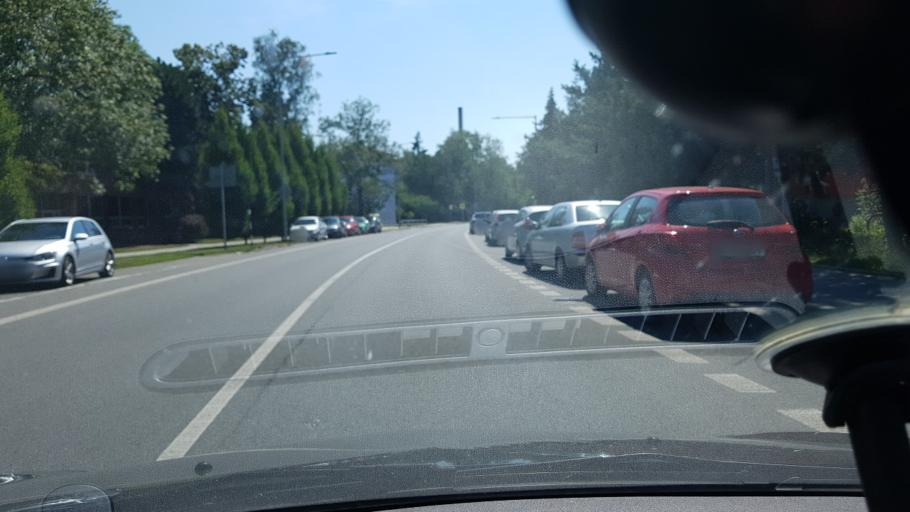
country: CZ
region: Moravskoslezsky
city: Bohumin
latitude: 49.9057
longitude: 18.3494
